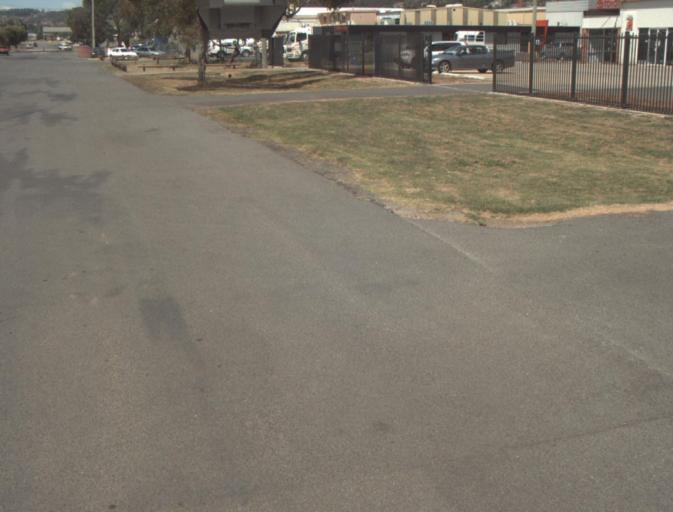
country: AU
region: Tasmania
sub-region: Launceston
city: Launceston
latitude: -41.4243
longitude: 147.1279
